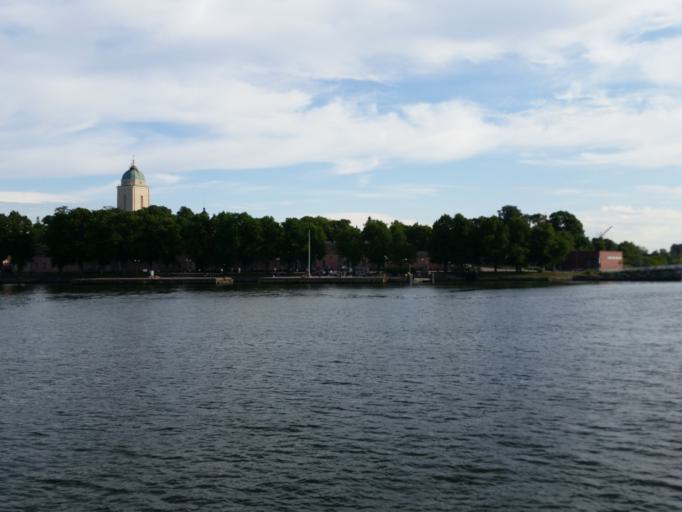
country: FI
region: Uusimaa
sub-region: Helsinki
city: Helsinki
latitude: 60.1510
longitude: 24.9840
